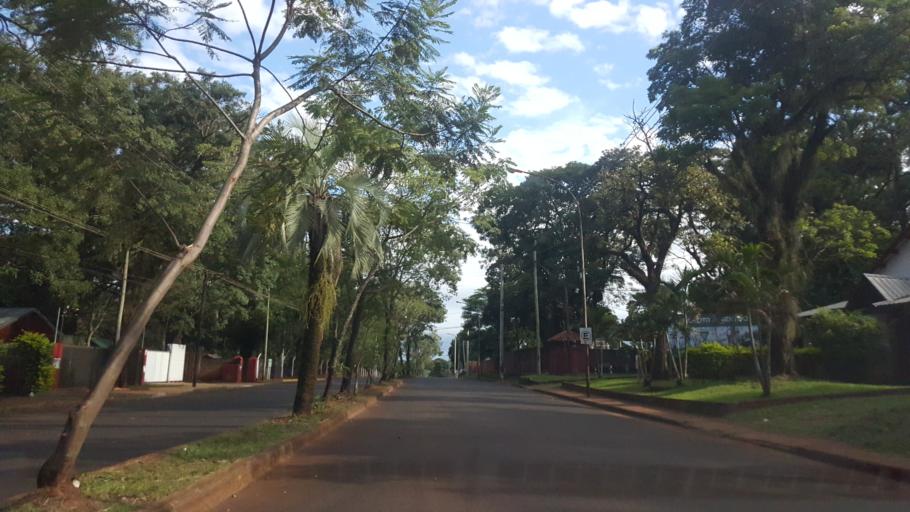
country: AR
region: Misiones
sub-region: Departamento de Capital
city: Posadas
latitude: -27.3628
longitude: -55.9160
